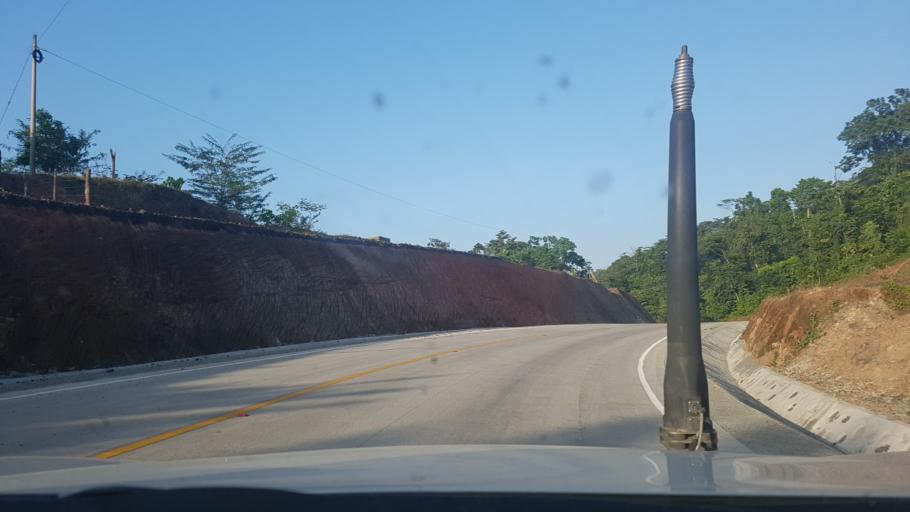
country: NI
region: Atlantico Sur
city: Rama
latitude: 11.8238
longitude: -84.0866
